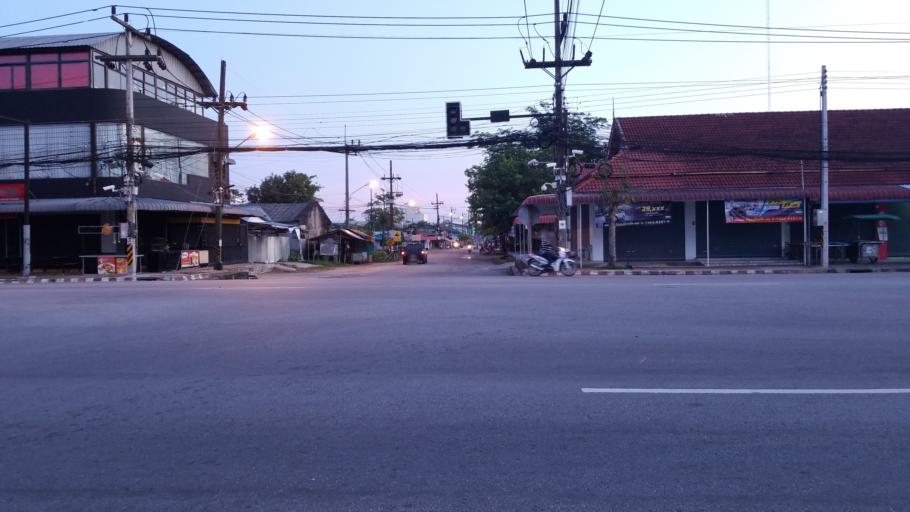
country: TH
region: Narathiwat
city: Su-ngai Kolok
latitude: 6.0243
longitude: 101.9614
